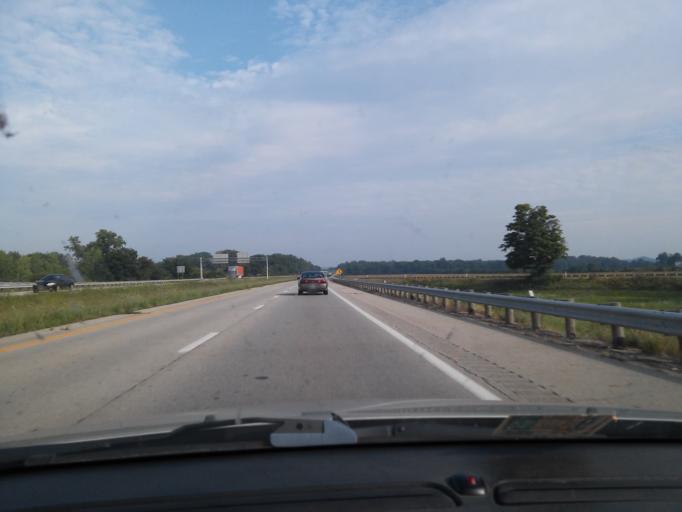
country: US
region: Ohio
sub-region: Ross County
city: Chillicothe
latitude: 39.3149
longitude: -82.9307
